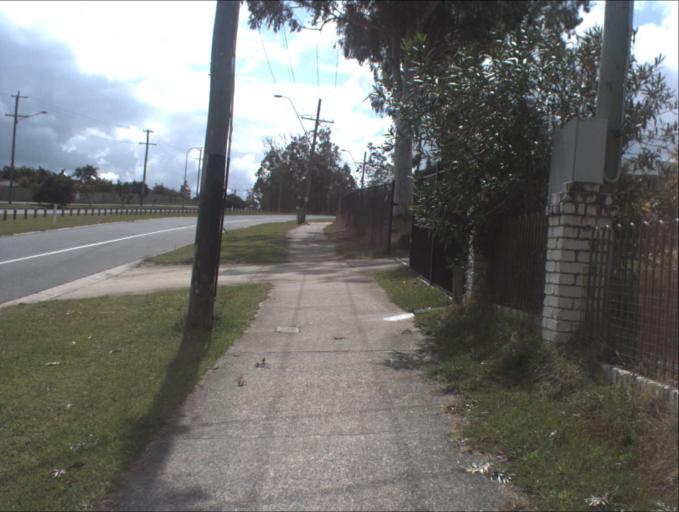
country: AU
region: Queensland
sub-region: Logan
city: Park Ridge South
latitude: -27.6842
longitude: 153.0589
